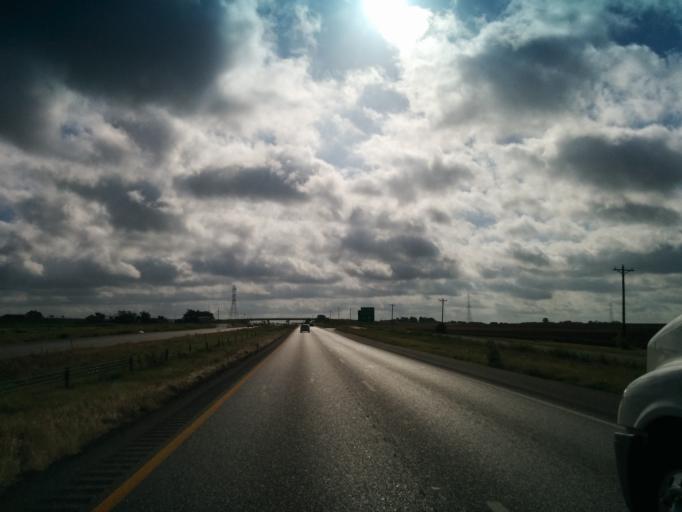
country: US
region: Texas
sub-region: Guadalupe County
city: Marion
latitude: 29.5345
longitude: -98.0914
